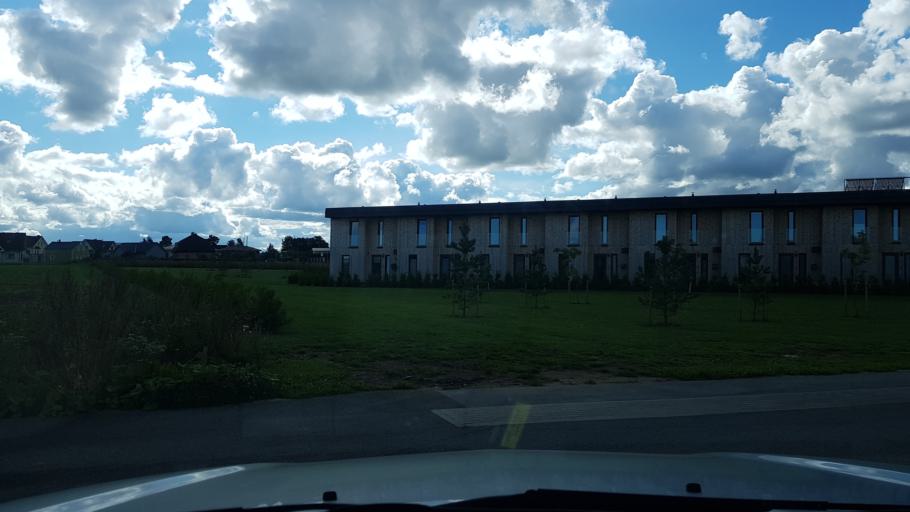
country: EE
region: Harju
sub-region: Tallinna linn
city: Tallinn
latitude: 59.3850
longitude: 24.8098
